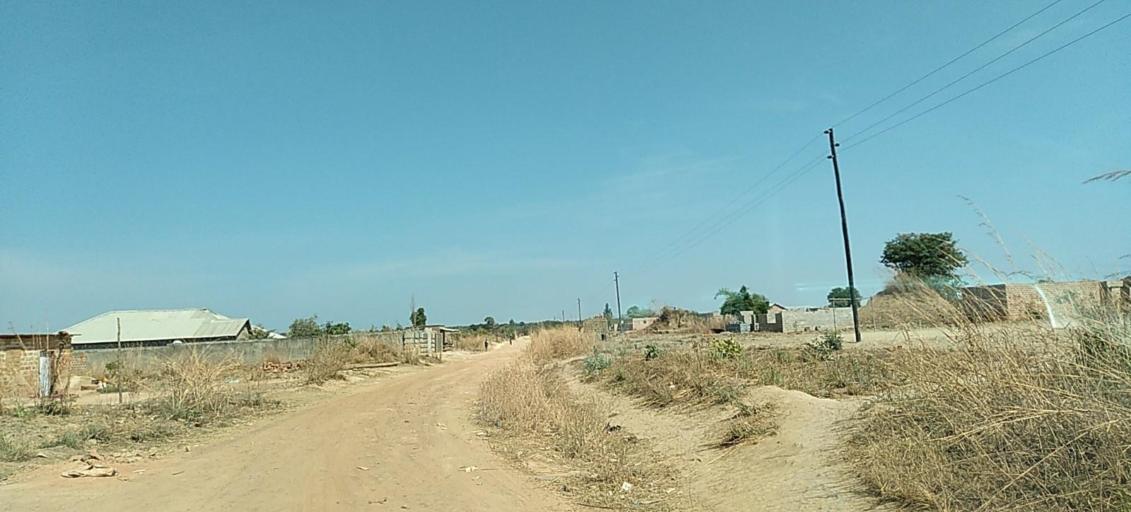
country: ZM
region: Copperbelt
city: Chililabombwe
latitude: -12.3381
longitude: 27.8661
